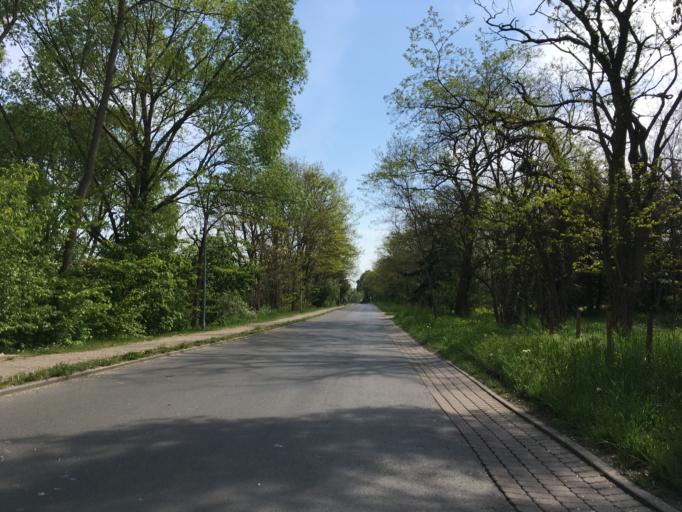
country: DE
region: Brandenburg
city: Werneuchen
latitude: 52.6004
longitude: 13.7490
